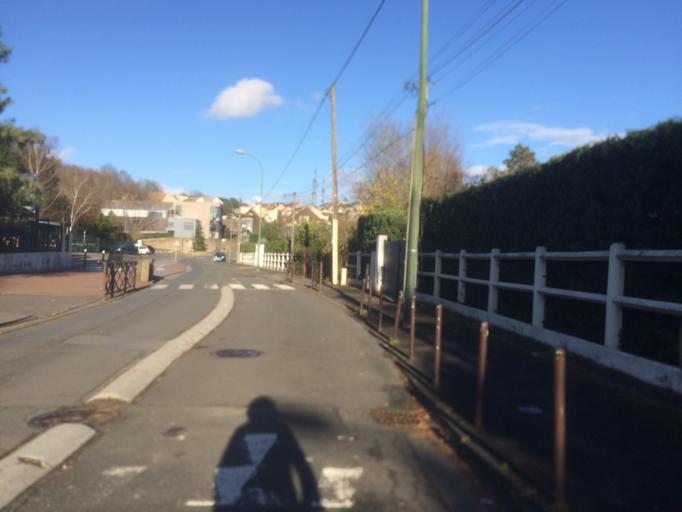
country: FR
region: Ile-de-France
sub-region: Departement de l'Essonne
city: Igny
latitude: 48.7375
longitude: 2.2201
